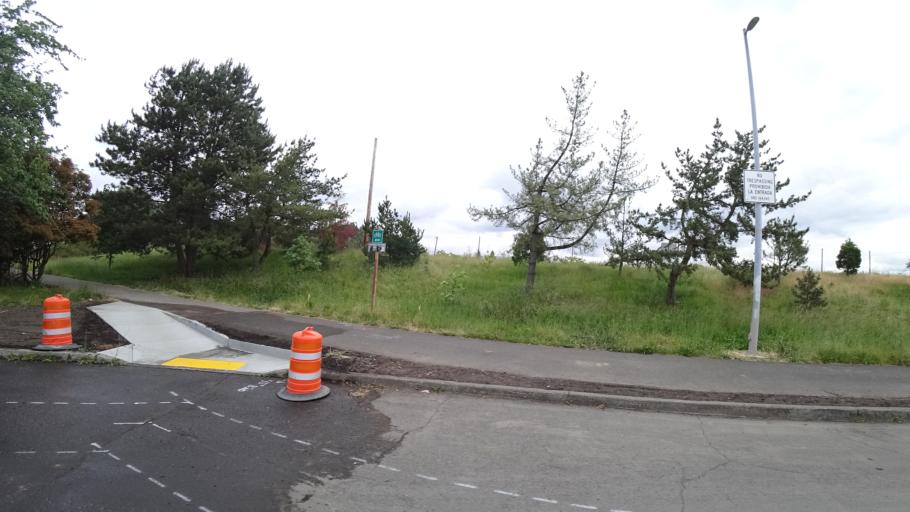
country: US
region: Oregon
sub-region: Multnomah County
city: Lents
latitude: 45.4944
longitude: -122.5673
